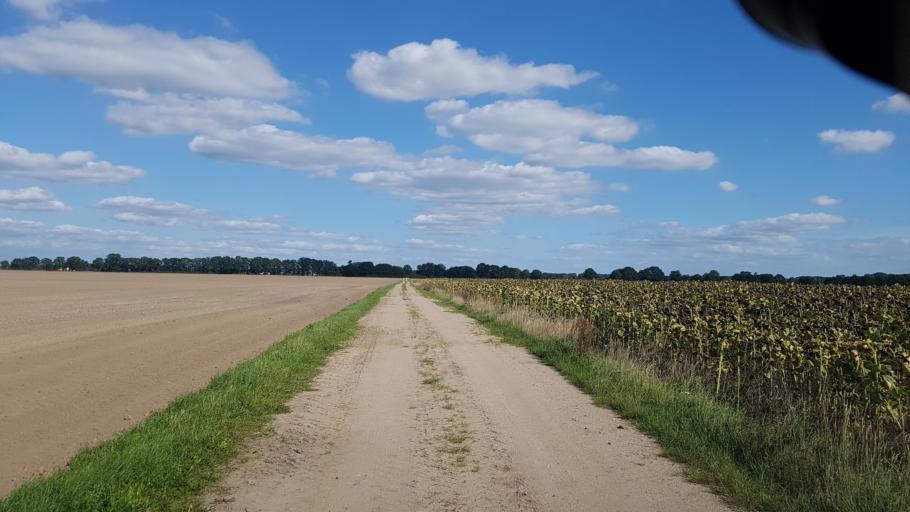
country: DE
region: Brandenburg
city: Sonnewalde
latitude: 51.6807
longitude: 13.6529
